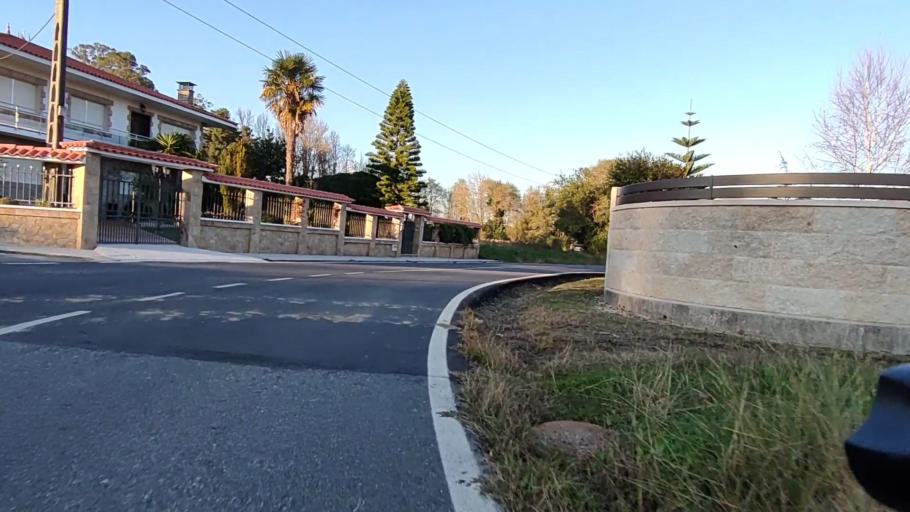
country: ES
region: Galicia
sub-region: Provincia da Coruna
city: Boiro
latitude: 42.6316
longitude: -8.8605
